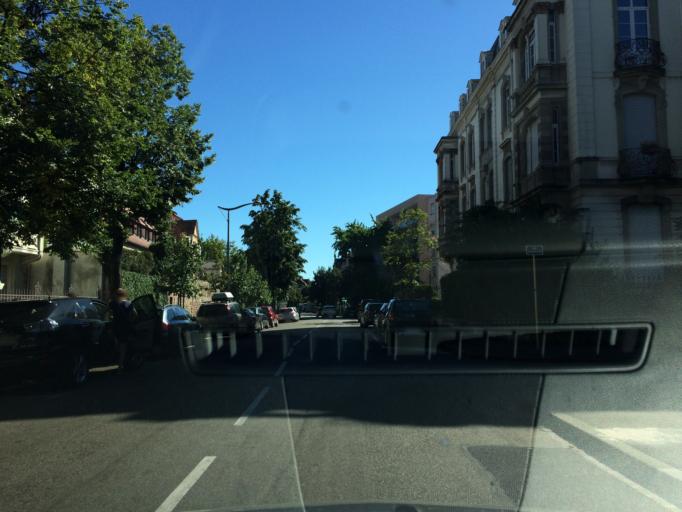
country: FR
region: Alsace
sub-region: Departement du Haut-Rhin
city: Colmar
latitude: 48.0753
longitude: 7.3547
